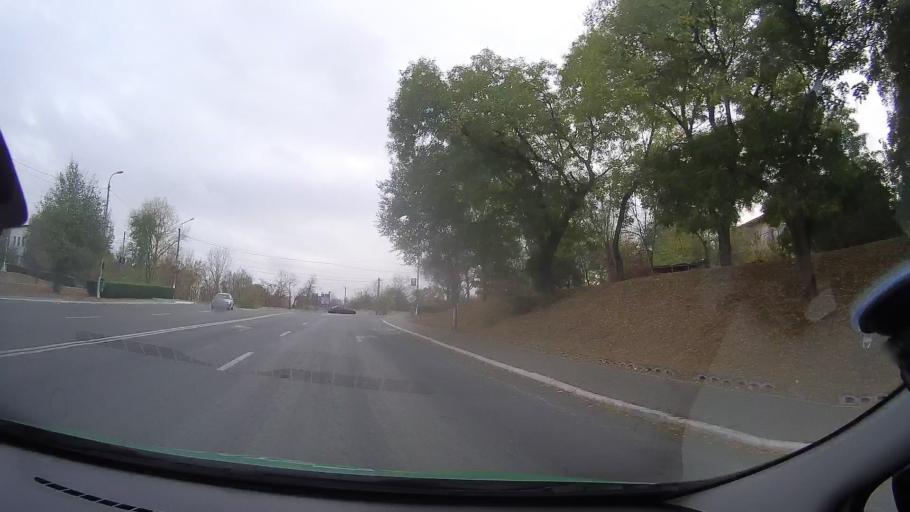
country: RO
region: Constanta
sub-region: Municipiul Medgidia
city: Medgidia
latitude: 44.2450
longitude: 28.2598
